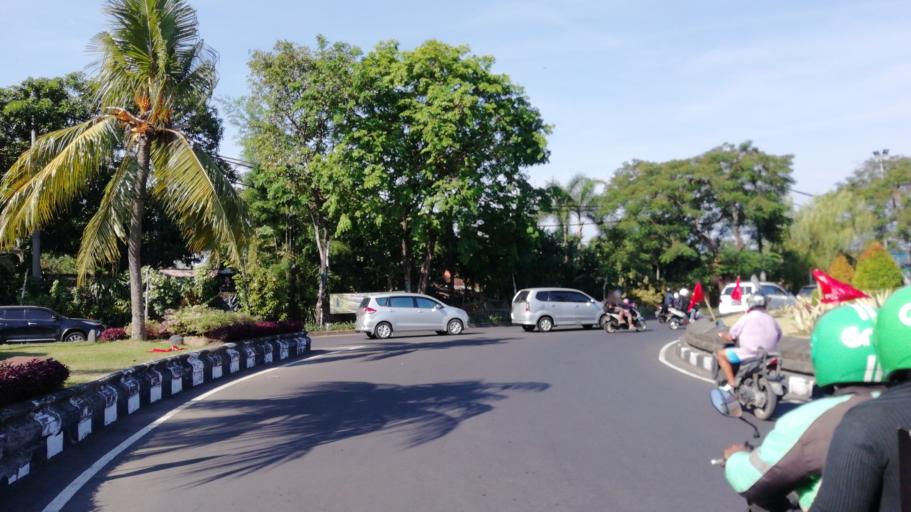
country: ID
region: Bali
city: Banjar Batanpoh
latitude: -8.6734
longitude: 115.2447
